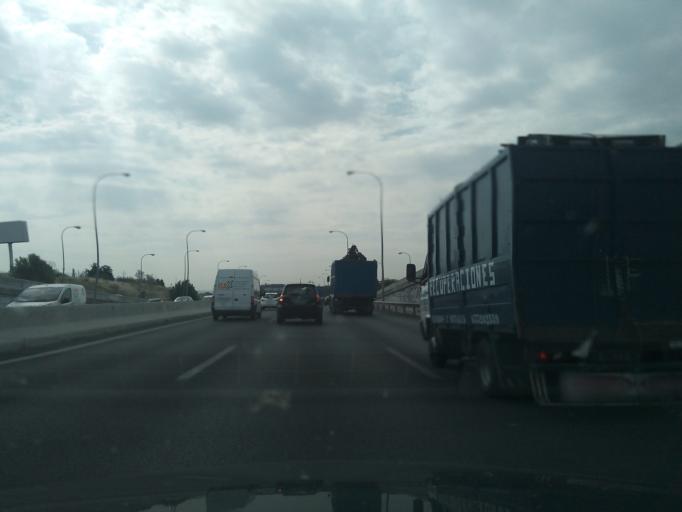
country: ES
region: Madrid
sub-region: Provincia de Madrid
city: San Blas
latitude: 40.4575
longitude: -3.6162
